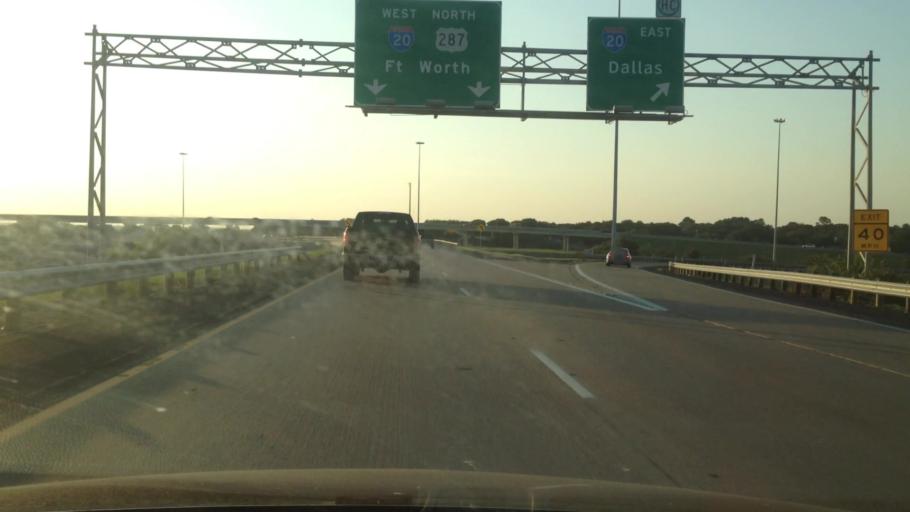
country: US
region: Texas
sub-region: Tarrant County
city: Kennedale
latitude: 32.6681
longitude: -97.2053
